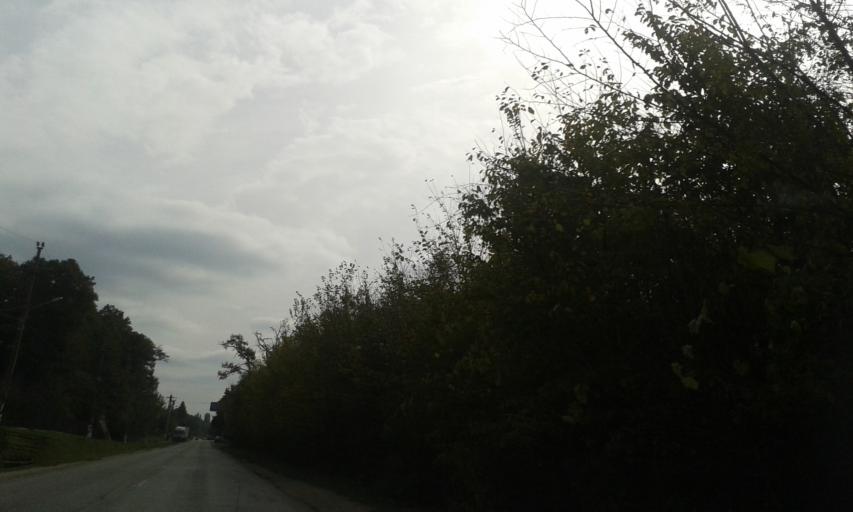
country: RO
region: Gorj
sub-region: Comuna Targu Carbunesti
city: Targu Carbunesti
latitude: 44.9664
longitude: 23.5046
